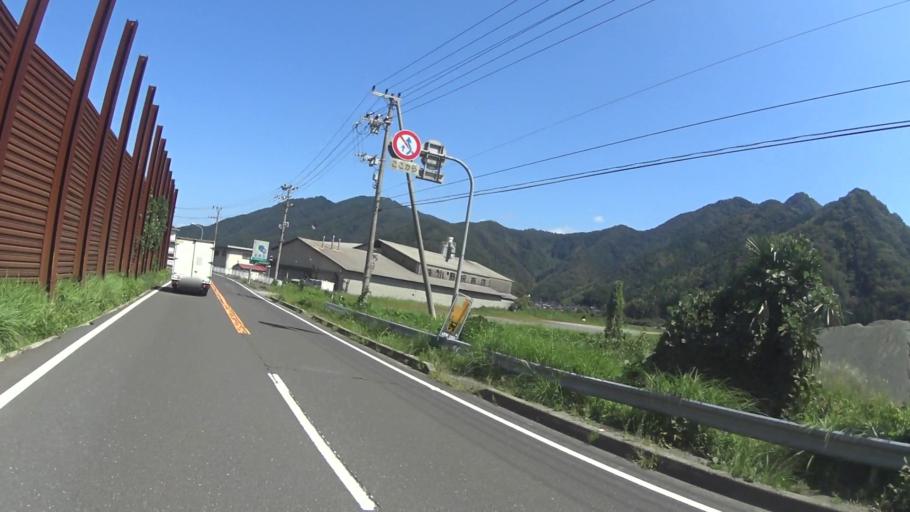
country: JP
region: Kyoto
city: Maizuru
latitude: 35.4898
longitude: 135.2816
